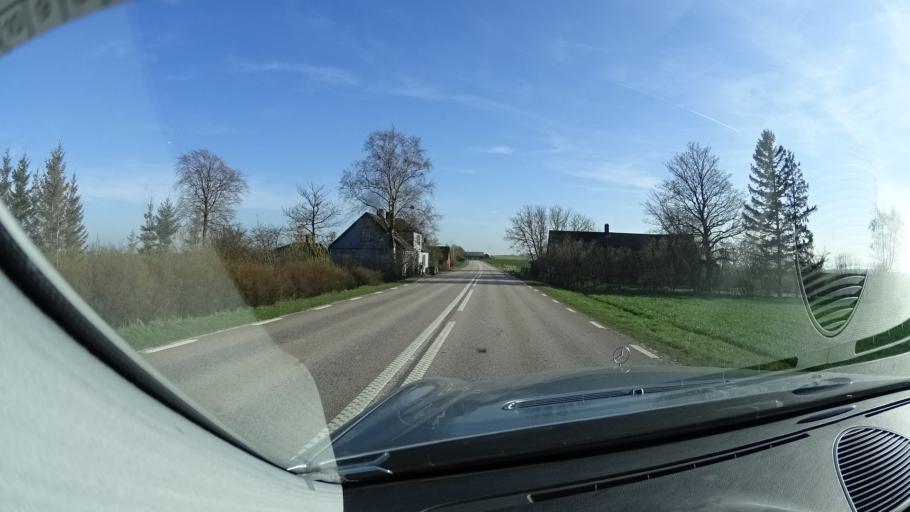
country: SE
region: Skane
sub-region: Landskrona
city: Asmundtorp
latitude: 55.9414
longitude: 12.9494
